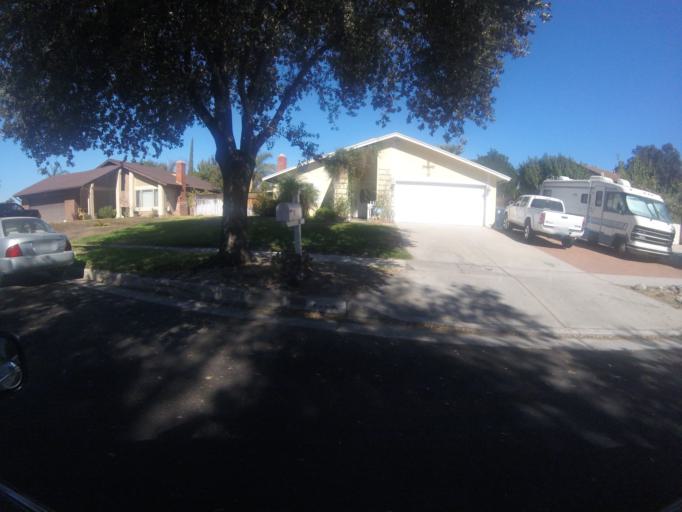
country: US
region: California
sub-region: San Bernardino County
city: Redlands
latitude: 34.0729
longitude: -117.1677
